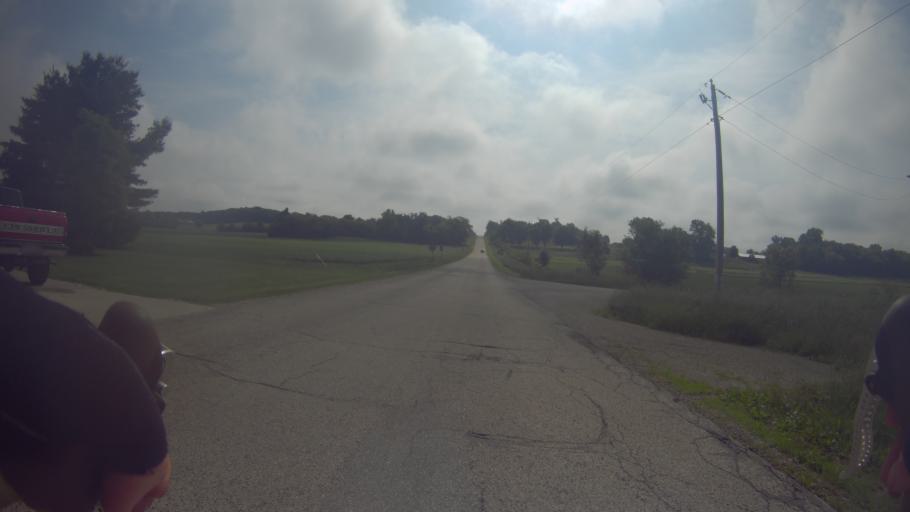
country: US
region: Wisconsin
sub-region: Dane County
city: Stoughton
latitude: 42.9411
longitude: -89.1718
